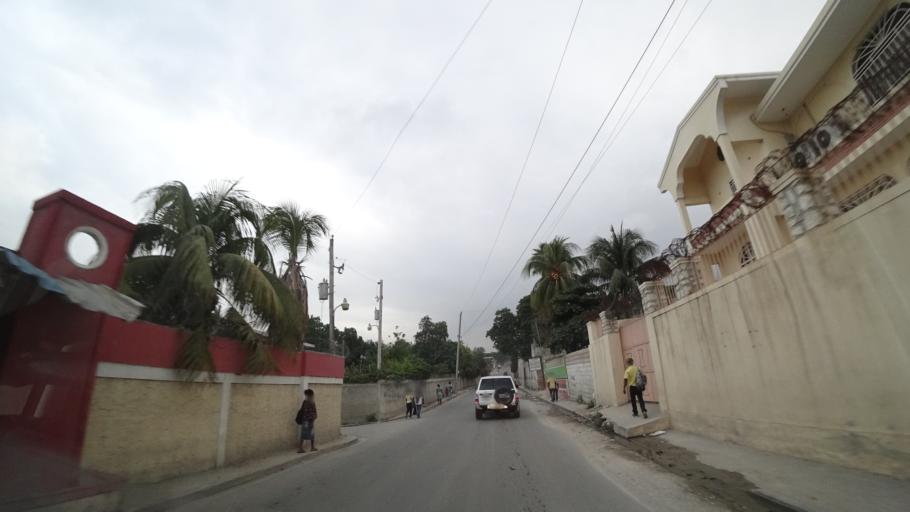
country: HT
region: Ouest
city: Delmas 73
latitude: 18.5684
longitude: -72.3006
